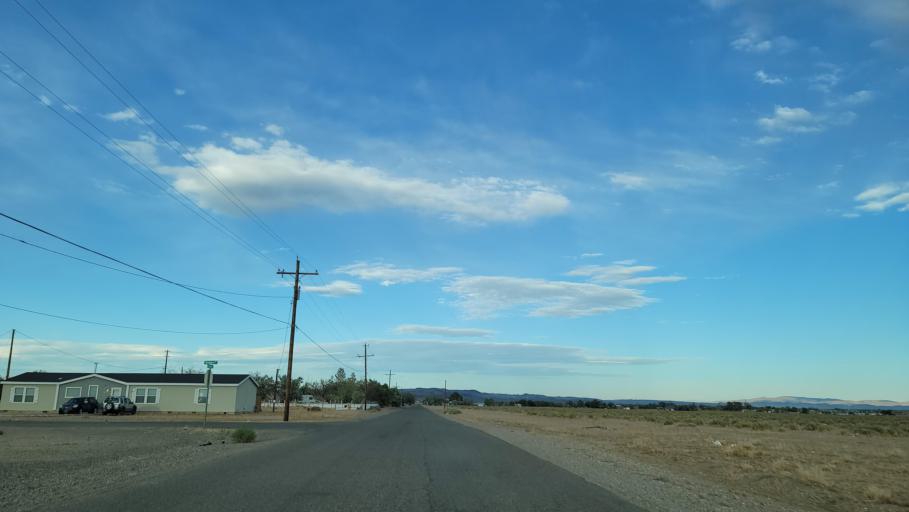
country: US
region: Nevada
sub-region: Lyon County
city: Silver Springs
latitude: 39.3899
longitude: -119.2477
